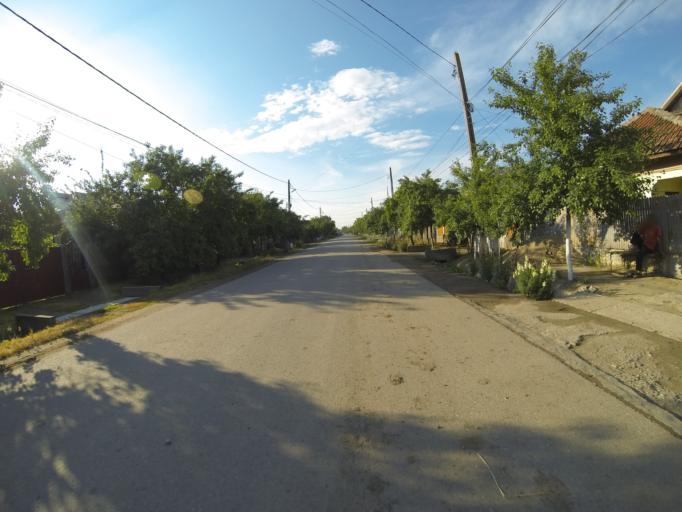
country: RO
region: Dolj
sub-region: Comuna Tuglui
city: Tuglui
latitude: 44.1810
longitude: 23.8148
